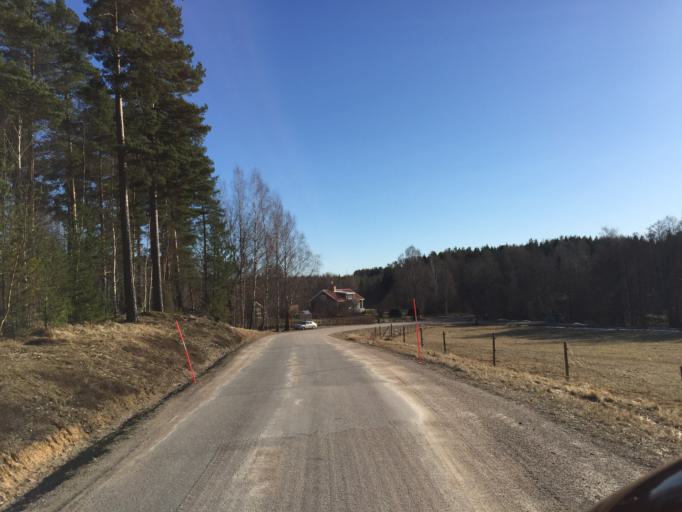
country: SE
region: Soedermanland
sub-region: Vingakers Kommun
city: Vingaker
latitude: 58.9509
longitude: 15.6667
